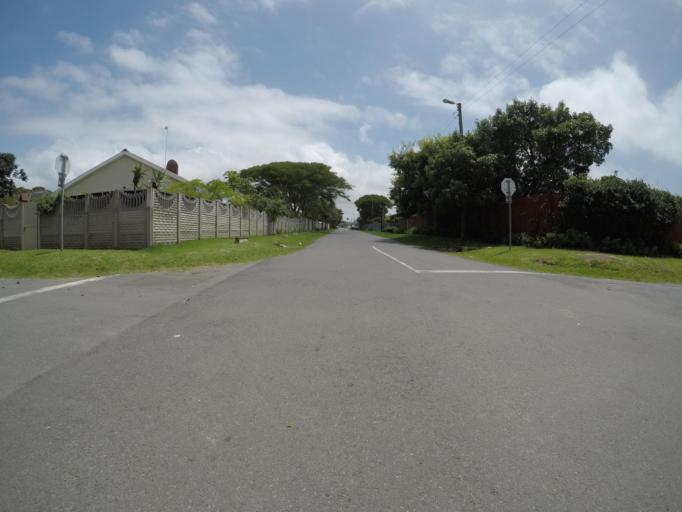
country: ZA
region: Eastern Cape
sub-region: Buffalo City Metropolitan Municipality
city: East London
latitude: -32.9412
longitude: 28.0118
